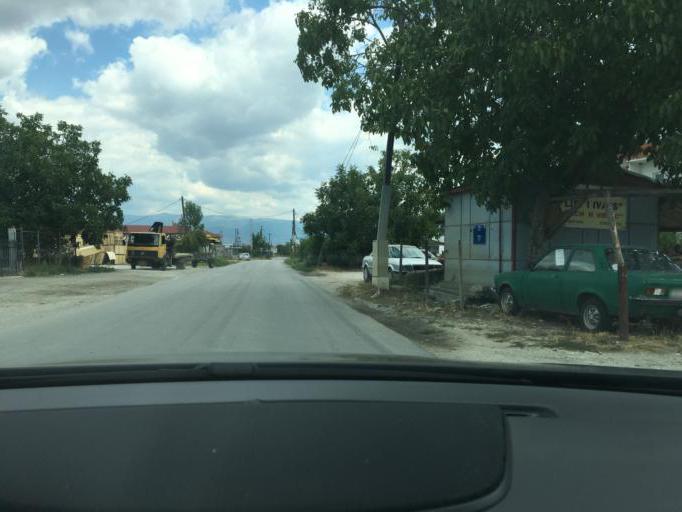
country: MK
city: Ljubin
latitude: 41.9922
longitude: 21.3167
